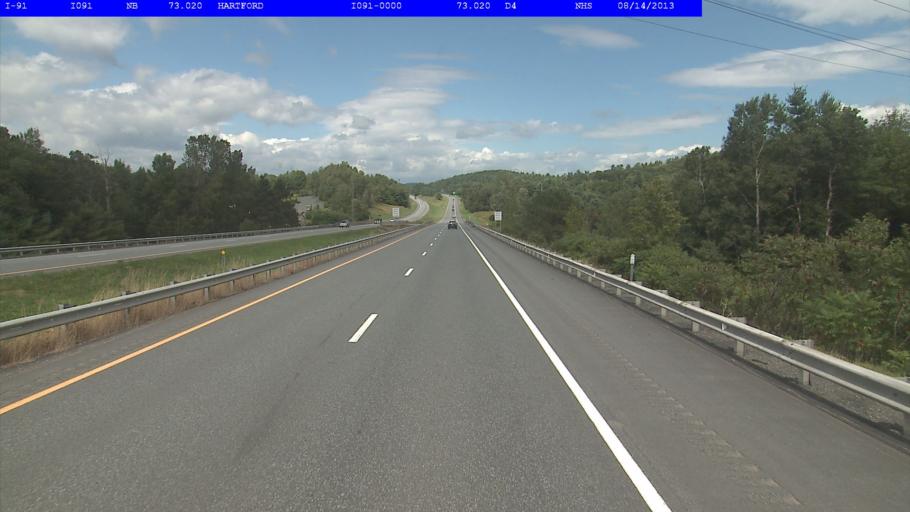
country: US
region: Vermont
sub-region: Windsor County
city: Wilder
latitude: 43.6807
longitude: -72.3159
